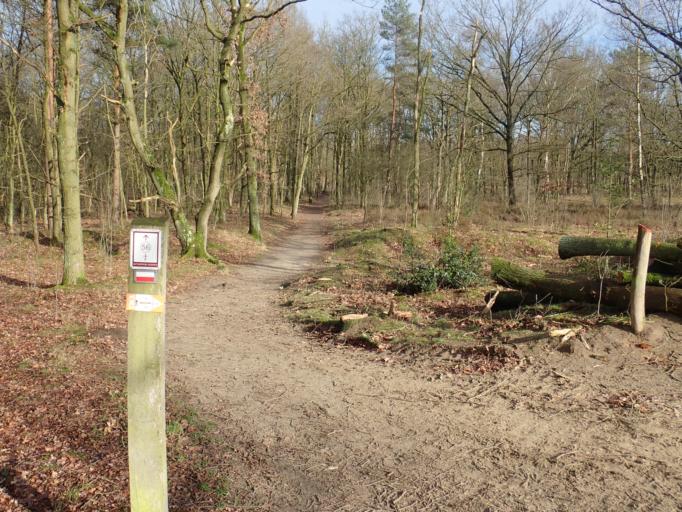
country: BE
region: Flanders
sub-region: Provincie Antwerpen
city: Nijlen
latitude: 51.1589
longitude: 4.6277
